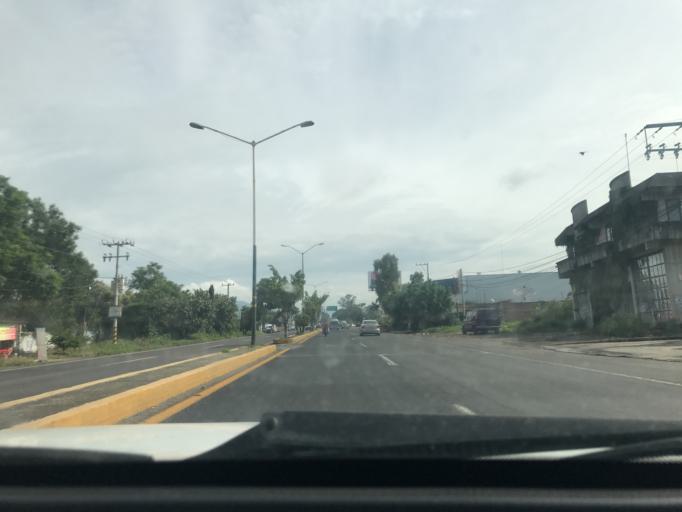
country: MX
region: Morelos
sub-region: Atlatlahucan
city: Colonia San Francisco
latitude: 18.8773
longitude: -98.9221
